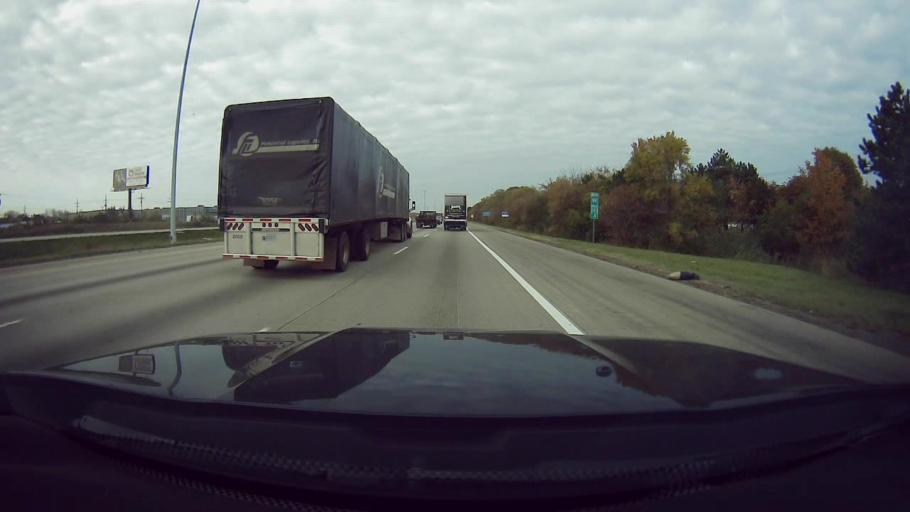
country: US
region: Michigan
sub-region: Wayne County
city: Allen Park
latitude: 42.2662
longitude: -83.2438
